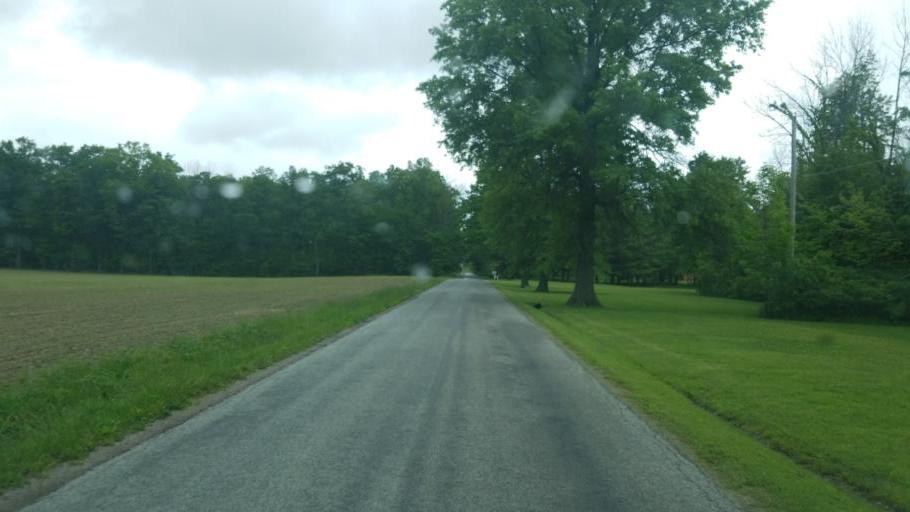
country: US
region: Ohio
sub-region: Crawford County
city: Crestline
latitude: 40.7448
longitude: -82.6888
